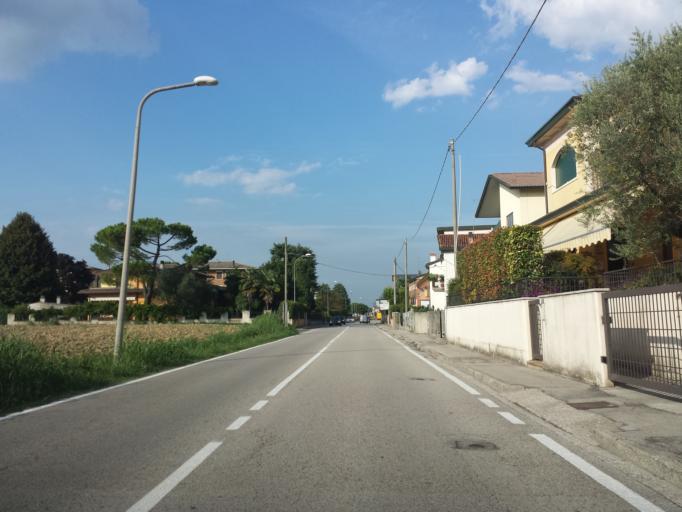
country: IT
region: Veneto
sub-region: Provincia di Vicenza
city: Torri di Quartesolo
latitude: 45.5209
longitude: 11.6066
